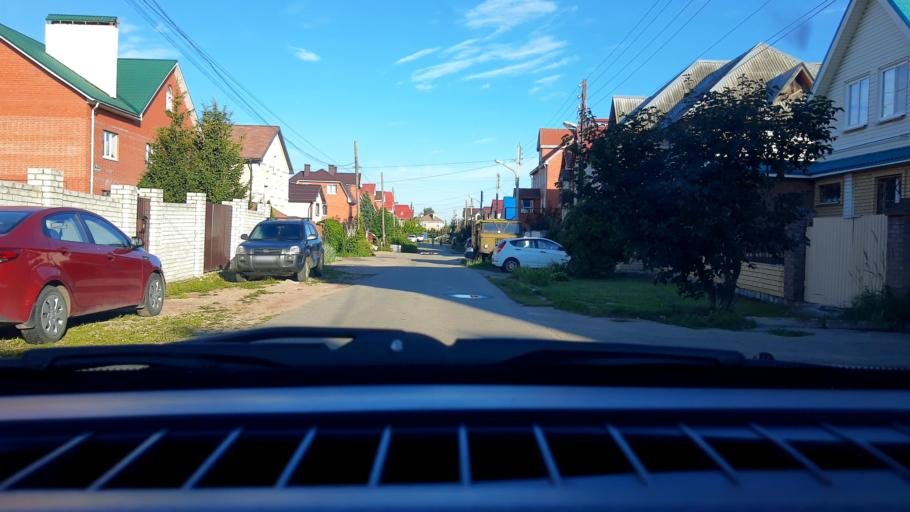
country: RU
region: Nizjnij Novgorod
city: Gorbatovka
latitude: 56.3714
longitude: 43.8354
